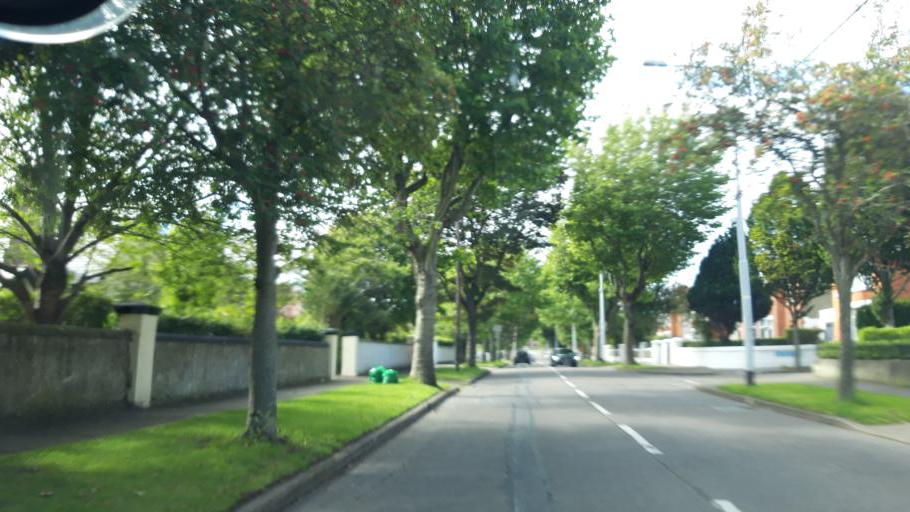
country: IE
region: Leinster
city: Dollymount
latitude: 53.3666
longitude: -6.1890
